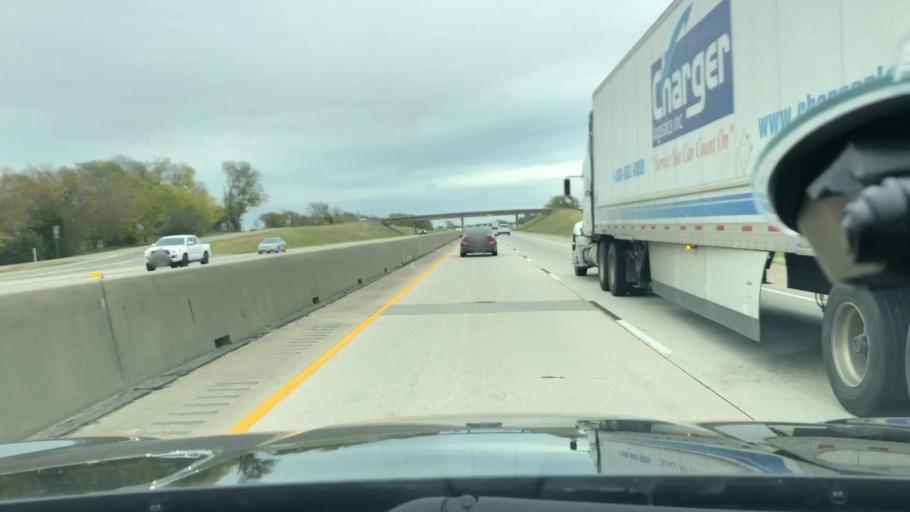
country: US
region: Texas
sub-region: Hopkins County
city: Sulphur Springs
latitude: 33.1245
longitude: -95.7370
